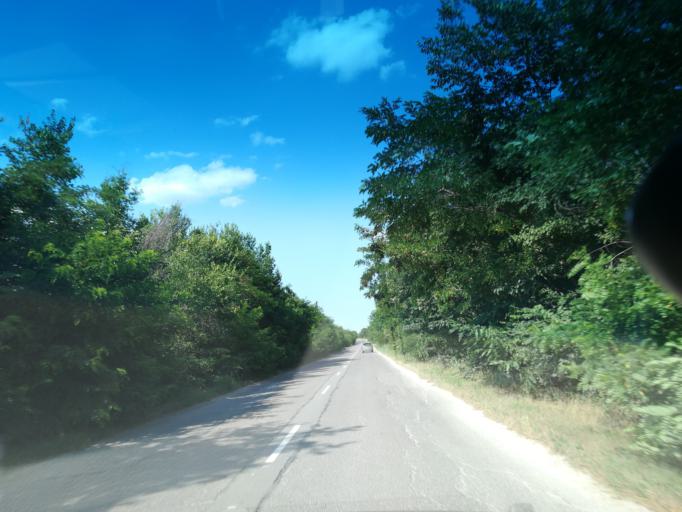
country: BG
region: Stara Zagora
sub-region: Obshtina Chirpan
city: Chirpan
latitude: 42.2441
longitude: 25.4077
